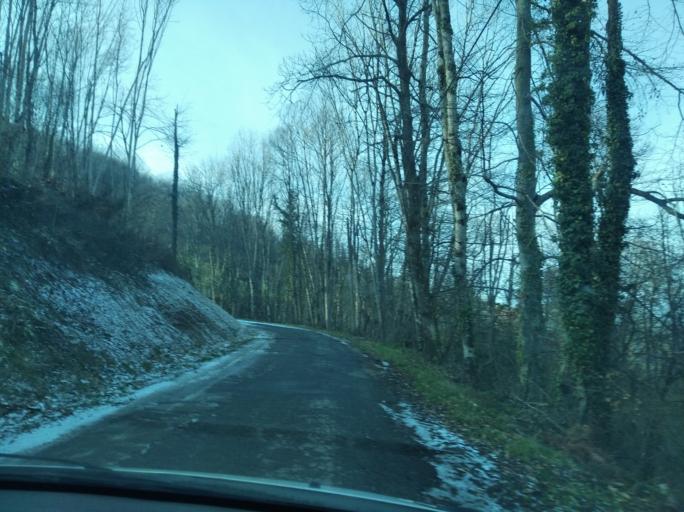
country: FR
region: Rhone-Alpes
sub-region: Departement de la Loire
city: La Pacaudiere
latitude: 46.1703
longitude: 3.7489
